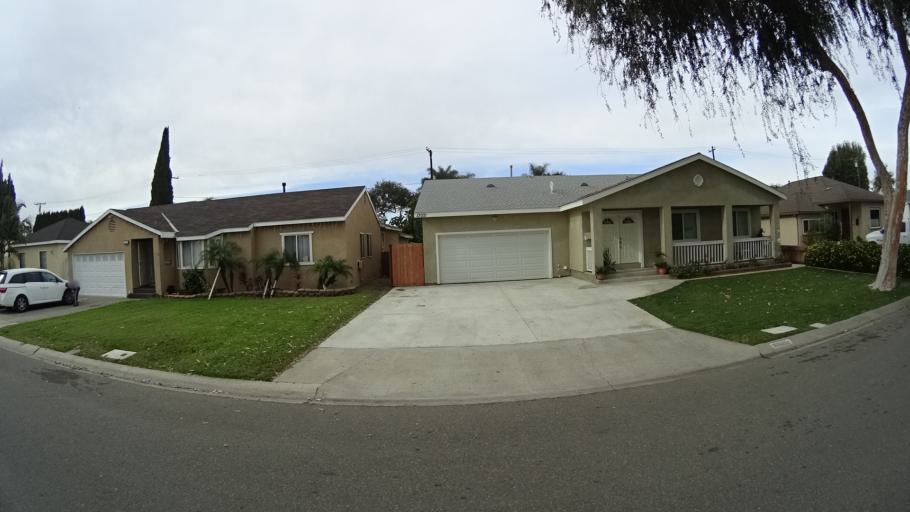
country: US
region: California
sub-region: Orange County
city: Garden Grove
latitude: 33.7729
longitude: -117.9319
